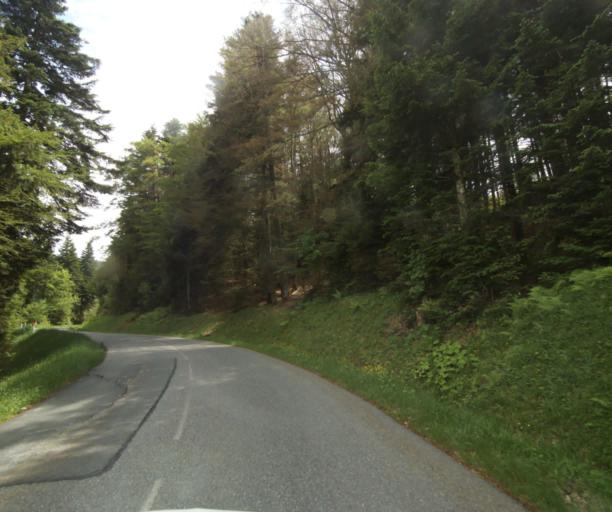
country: FR
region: Rhone-Alpes
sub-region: Departement de la Haute-Savoie
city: Perrignier
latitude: 46.2663
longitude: 6.4431
